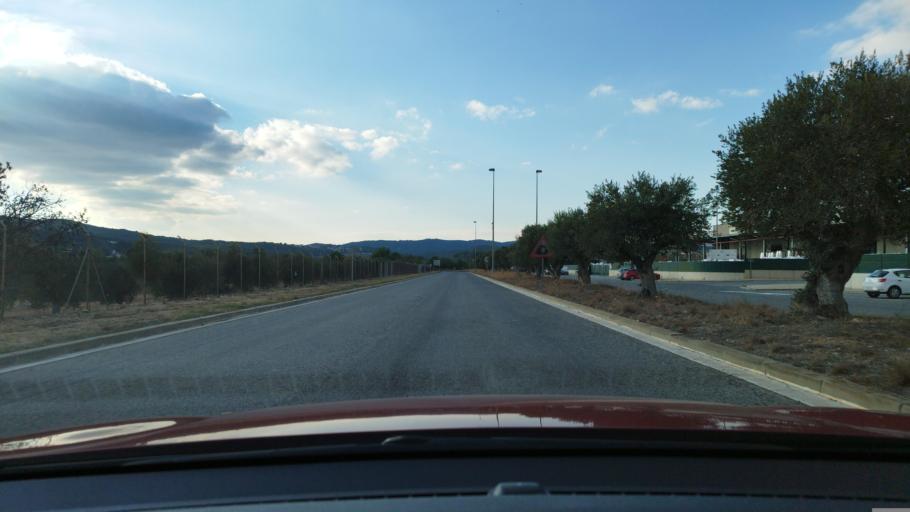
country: ES
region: Catalonia
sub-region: Provincia de Tarragona
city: la Bisbal del Penedes
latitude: 41.2693
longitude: 1.5079
